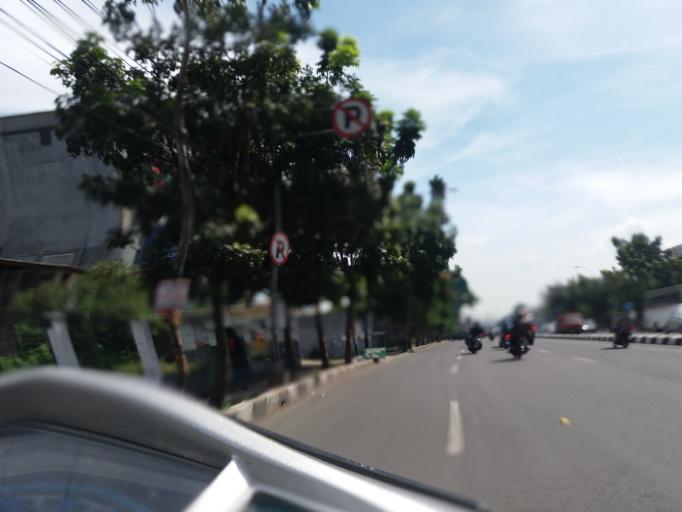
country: ID
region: West Java
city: Margahayukencana
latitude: -6.9464
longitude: 107.5912
